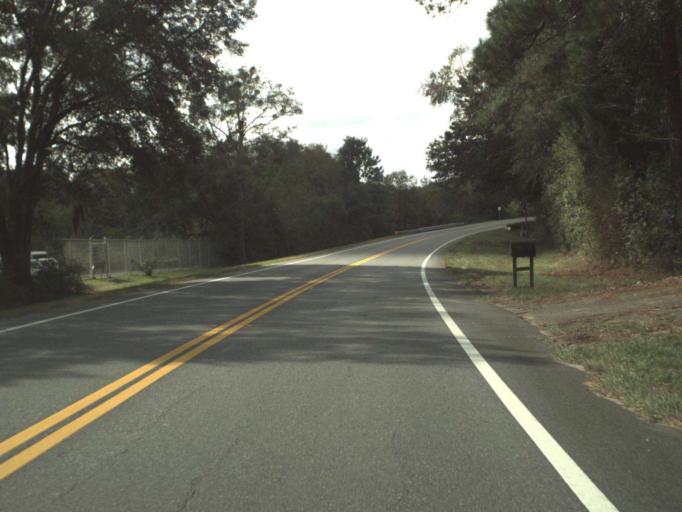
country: US
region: Florida
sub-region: Washington County
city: Chipley
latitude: 30.7925
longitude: -85.5261
